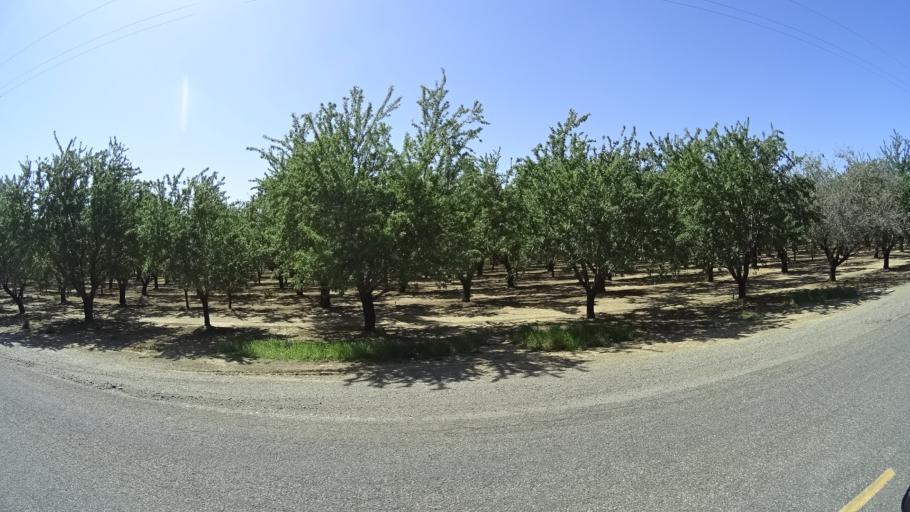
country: US
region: California
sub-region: Glenn County
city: Orland
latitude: 39.7111
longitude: -122.1870
